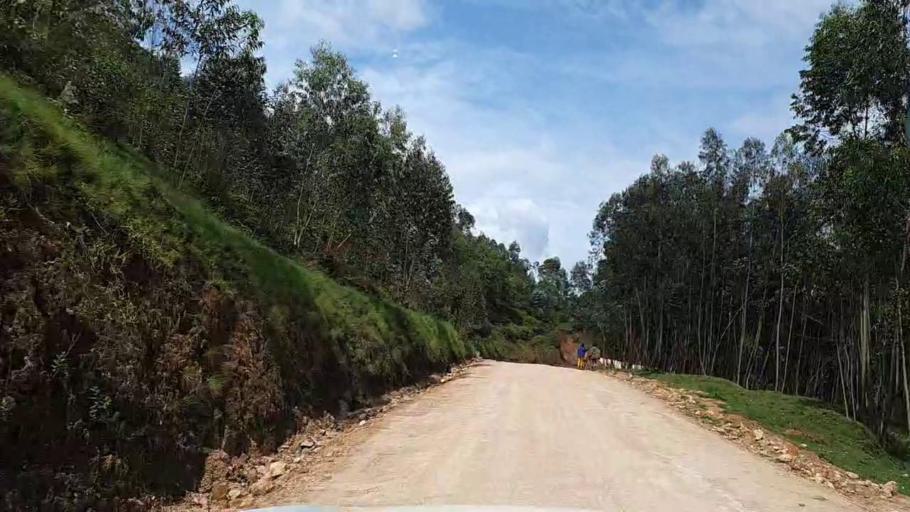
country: RW
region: Southern Province
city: Nzega
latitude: -2.3407
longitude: 29.4376
